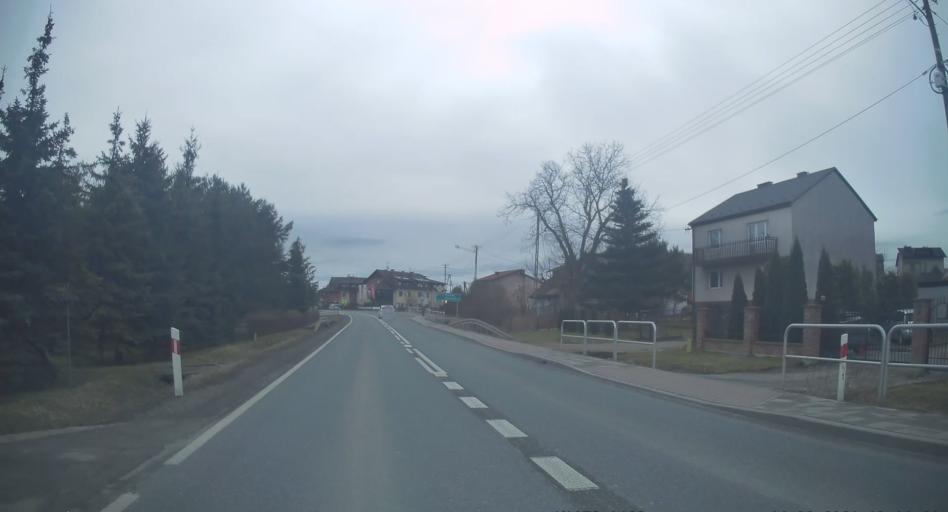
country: PL
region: Lesser Poland Voivodeship
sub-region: Powiat wielicki
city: Szarow
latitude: 50.0018
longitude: 20.2694
